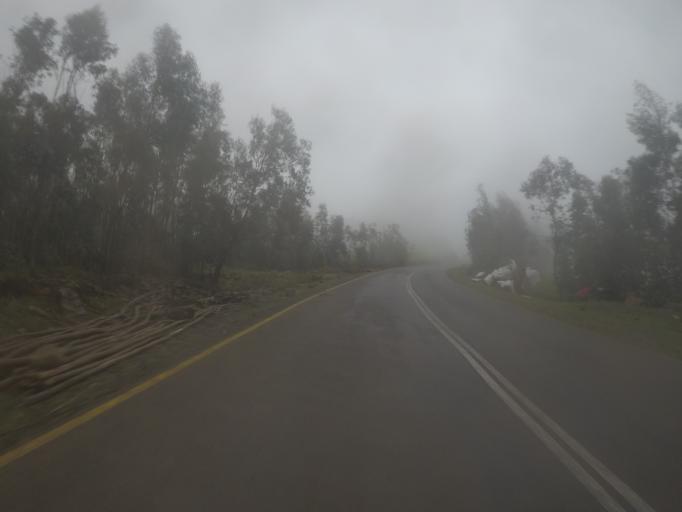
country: ET
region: Amhara
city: Gondar
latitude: 12.7244
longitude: 37.5001
